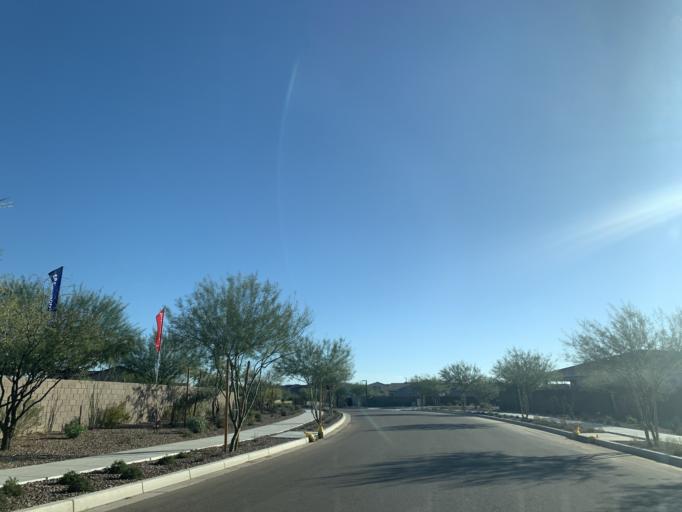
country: US
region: Arizona
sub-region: Maricopa County
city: Cave Creek
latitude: 33.6901
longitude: -112.0202
